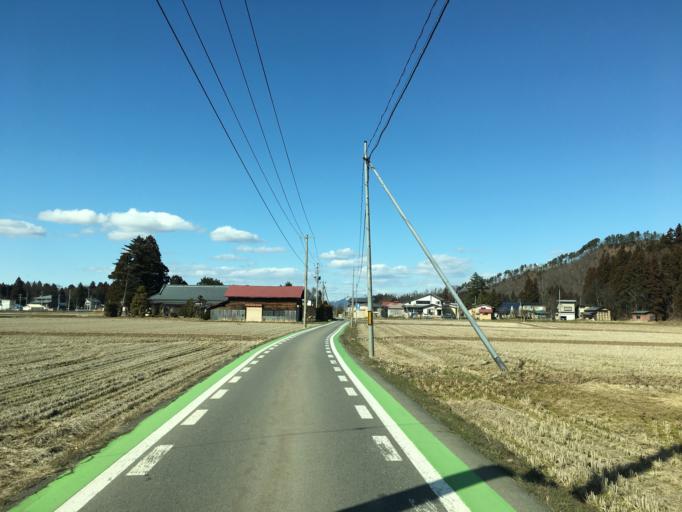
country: JP
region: Yamagata
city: Yonezawa
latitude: 37.9417
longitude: 140.1384
